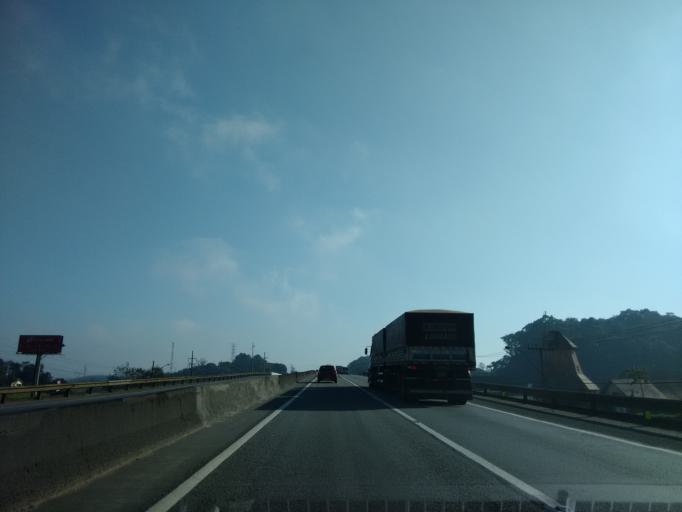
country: BR
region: Santa Catarina
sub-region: Joinville
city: Joinville
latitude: -26.2977
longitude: -48.8838
